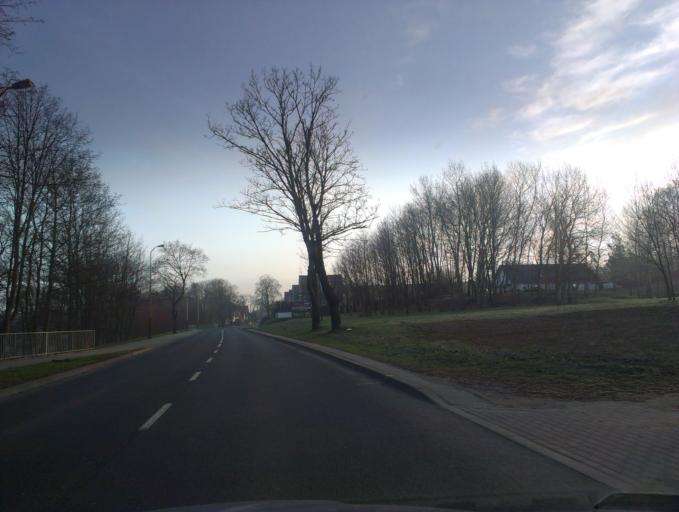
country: PL
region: West Pomeranian Voivodeship
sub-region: Powiat szczecinecki
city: Szczecinek
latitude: 53.6868
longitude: 16.6914
